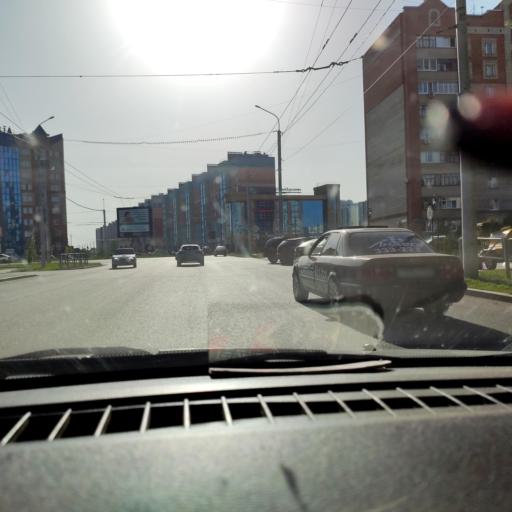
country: RU
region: Bashkortostan
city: Sterlitamak
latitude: 53.6377
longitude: 55.9023
